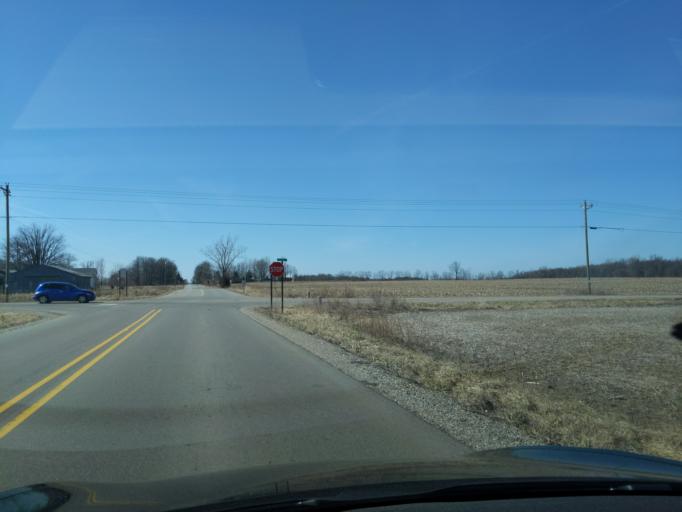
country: US
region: Michigan
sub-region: Eaton County
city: Grand Ledge
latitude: 42.7266
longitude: -84.8366
